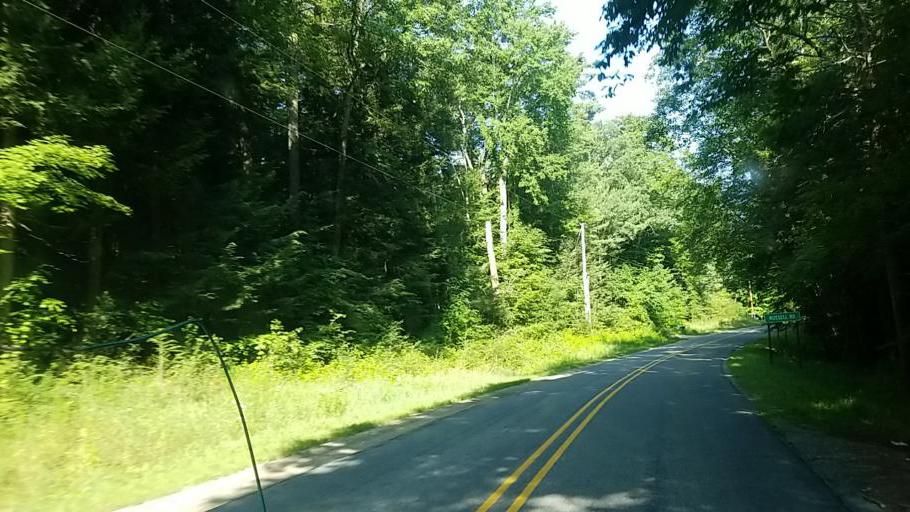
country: US
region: Michigan
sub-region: Muskegon County
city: Lakewood Club
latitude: 43.4626
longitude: -86.2268
